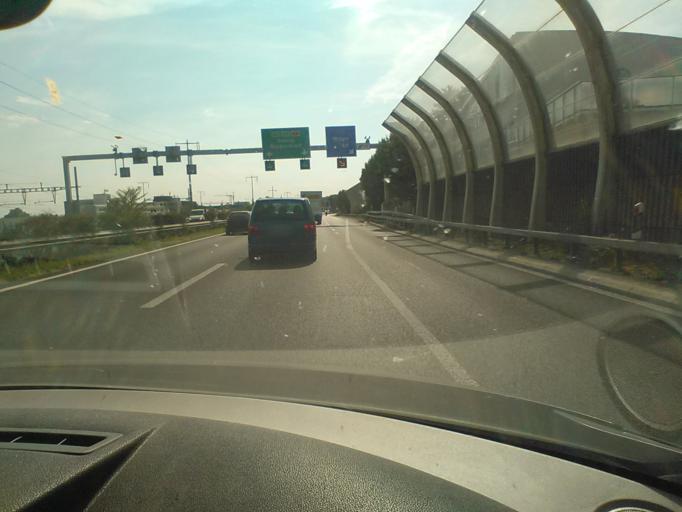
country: CH
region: Vaud
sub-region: Morges District
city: Morges
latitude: 46.5182
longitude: 6.5076
